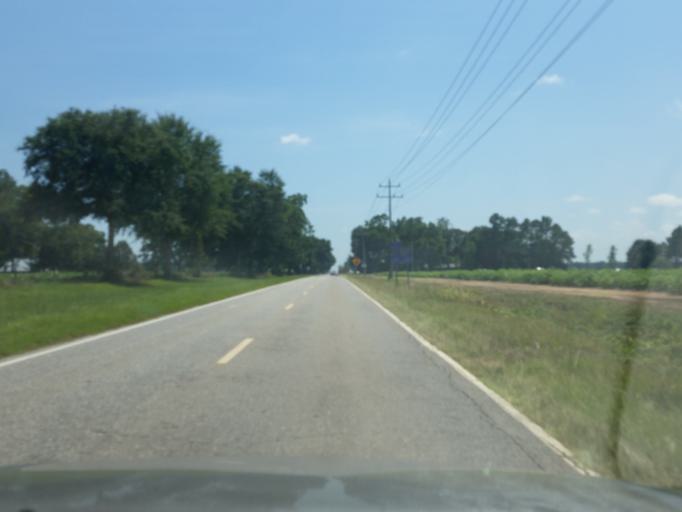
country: US
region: Alabama
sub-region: Baldwin County
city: Robertsdale
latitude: 30.6210
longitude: -87.6661
